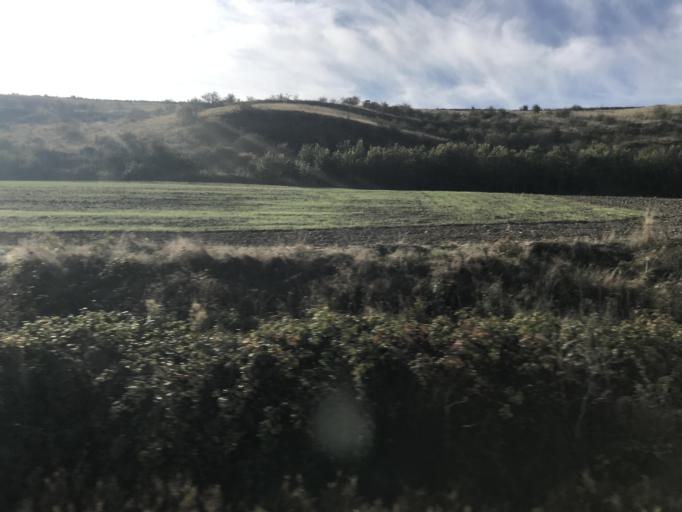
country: ES
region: Castille and Leon
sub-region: Provincia de Burgos
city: Cubo de Bureba
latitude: 42.6247
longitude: -3.1923
